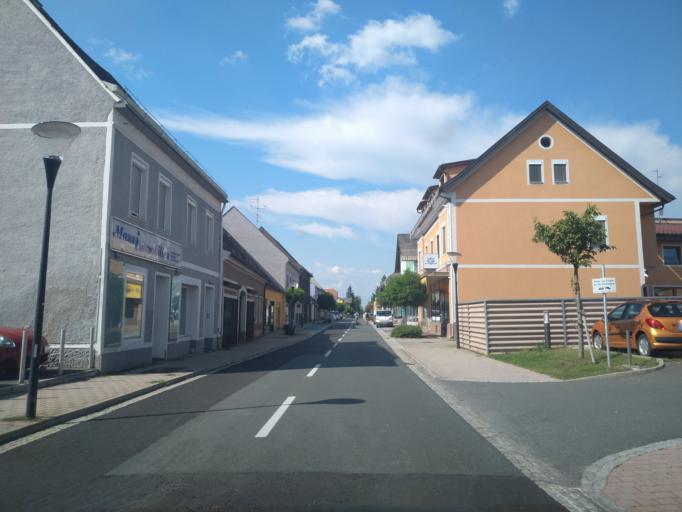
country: AT
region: Styria
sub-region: Politischer Bezirk Leibnitz
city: Leibnitz
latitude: 46.7845
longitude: 15.5391
